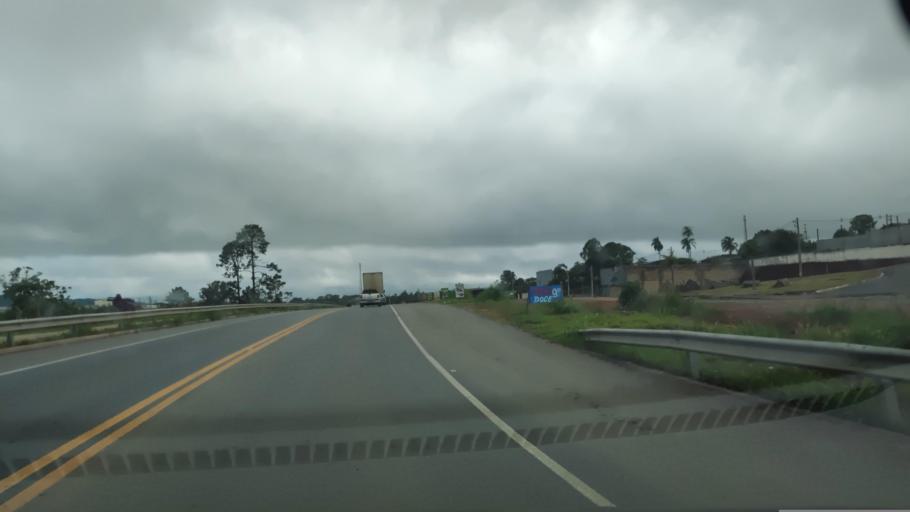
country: BR
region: Sao Paulo
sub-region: Vargem Grande Paulista
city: Vargem Grande Paulista
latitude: -23.6415
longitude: -47.0571
